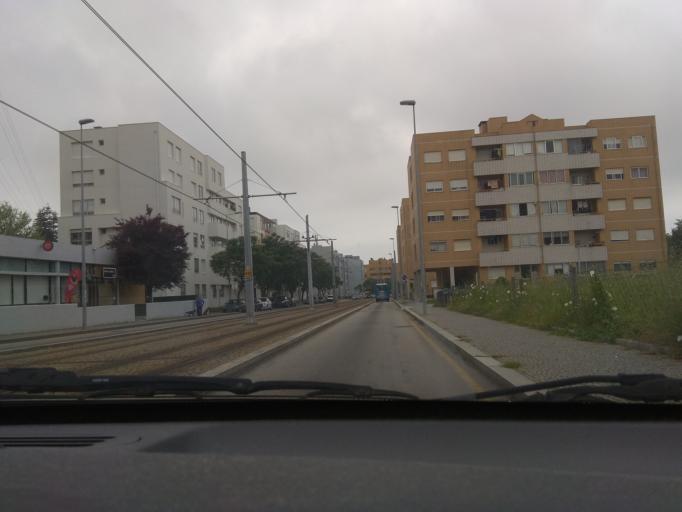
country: PT
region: Porto
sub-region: Matosinhos
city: Senhora da Hora
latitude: 41.1913
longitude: -8.6587
